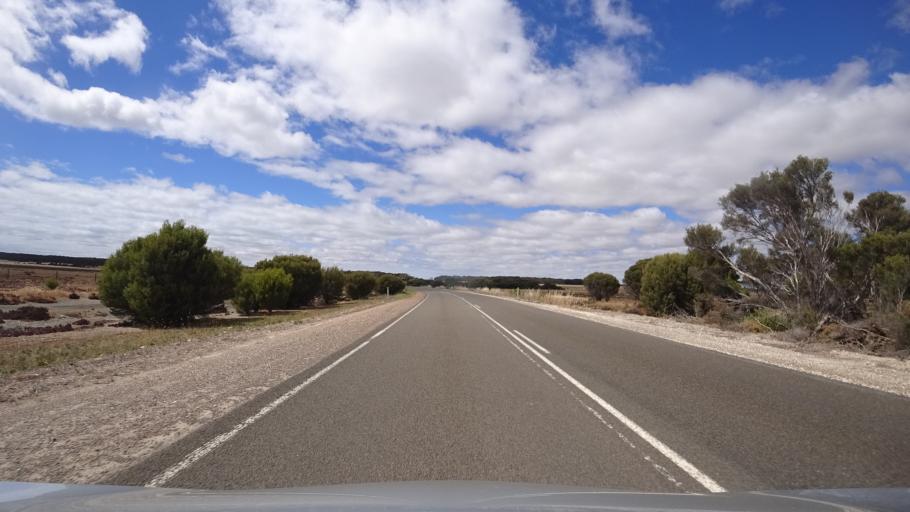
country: AU
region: South Australia
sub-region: Kangaroo Island
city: Kingscote
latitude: -35.6422
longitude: 137.5576
